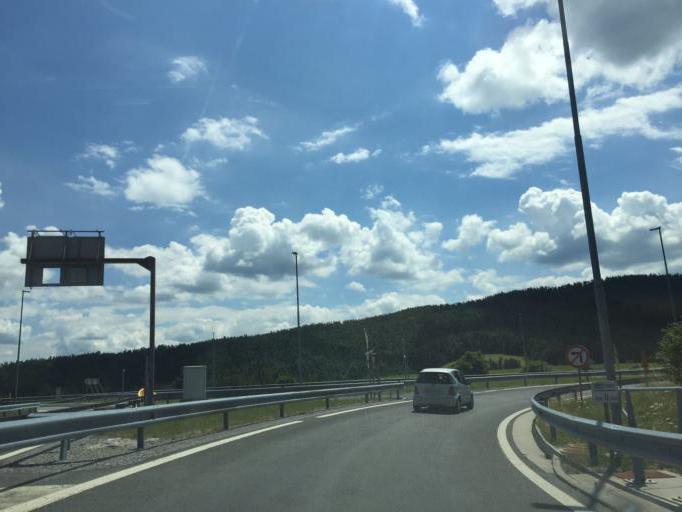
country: SI
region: Divaca
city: Divaca
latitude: 45.7601
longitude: 14.0760
